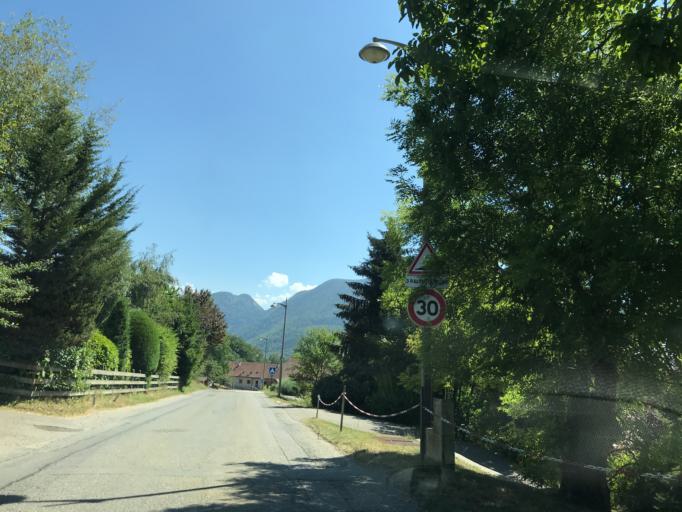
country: FR
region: Rhone-Alpes
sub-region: Departement de la Haute-Savoie
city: Villaz
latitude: 45.9391
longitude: 6.1930
